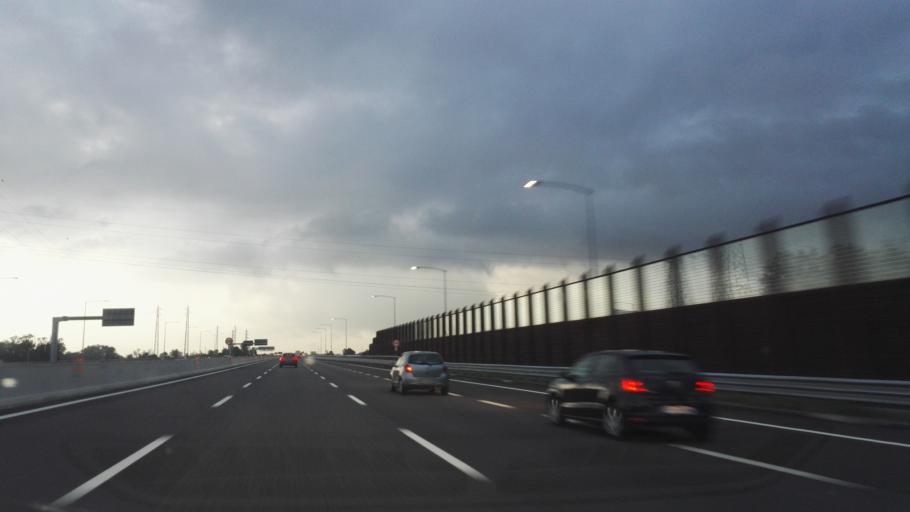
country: IT
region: Lombardy
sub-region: Citta metropolitana di Milano
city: Pozzuolo Martesana
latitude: 45.5190
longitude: 9.4403
